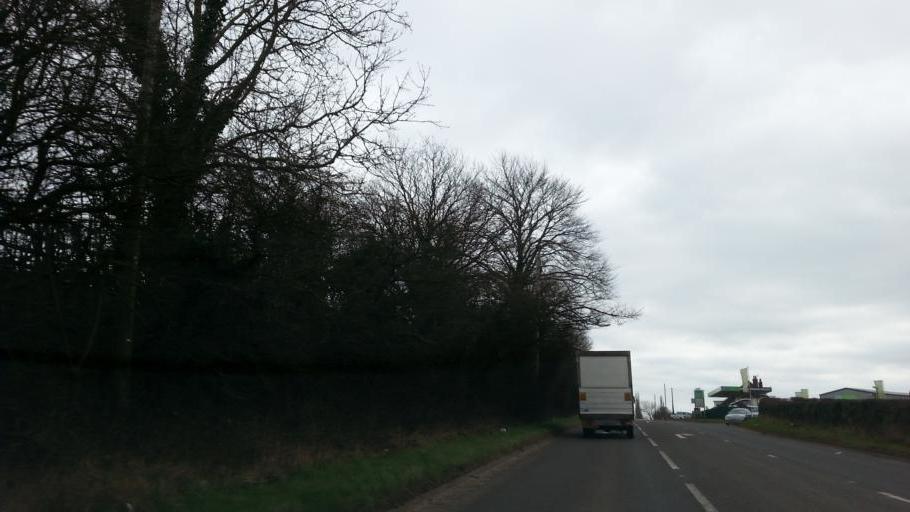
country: GB
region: England
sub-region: Staffordshire
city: Stone
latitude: 52.8768
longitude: -2.1040
